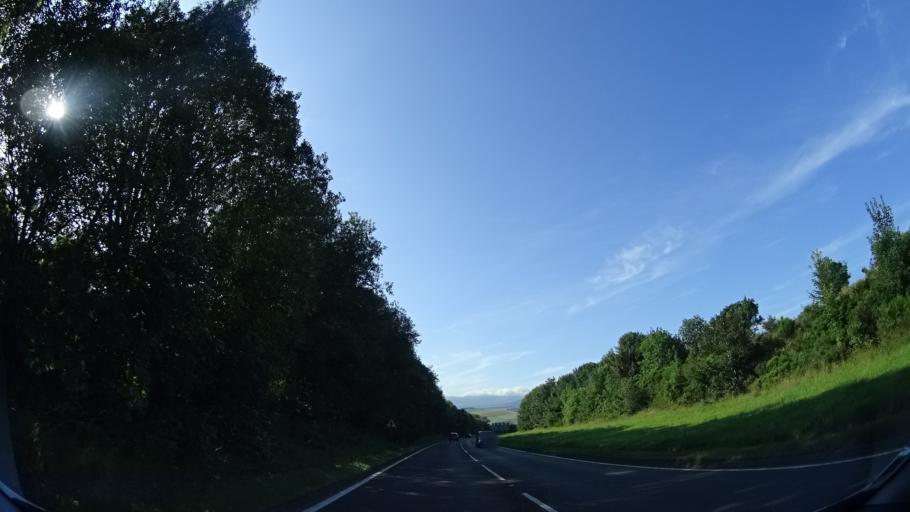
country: GB
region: Scotland
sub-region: Highland
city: Conon Bridge
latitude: 57.5541
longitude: -4.4139
